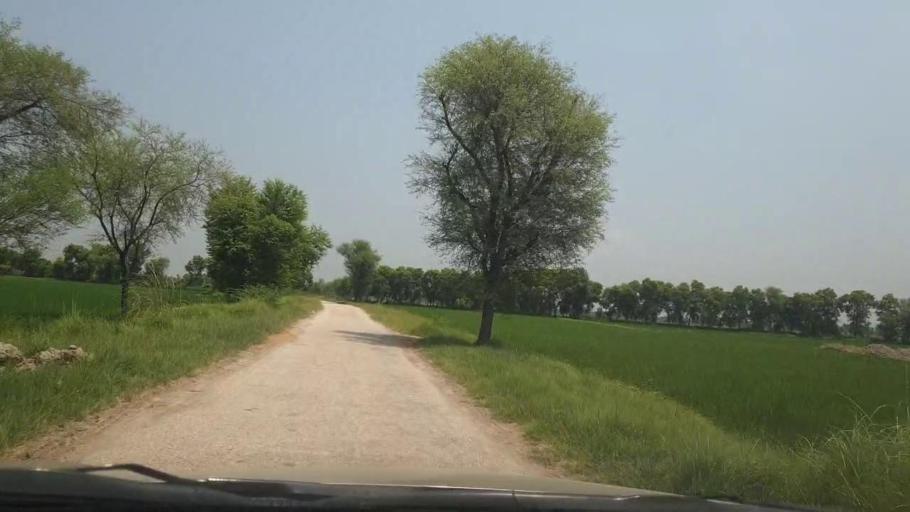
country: PK
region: Sindh
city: Ratodero
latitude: 27.7308
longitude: 68.2856
